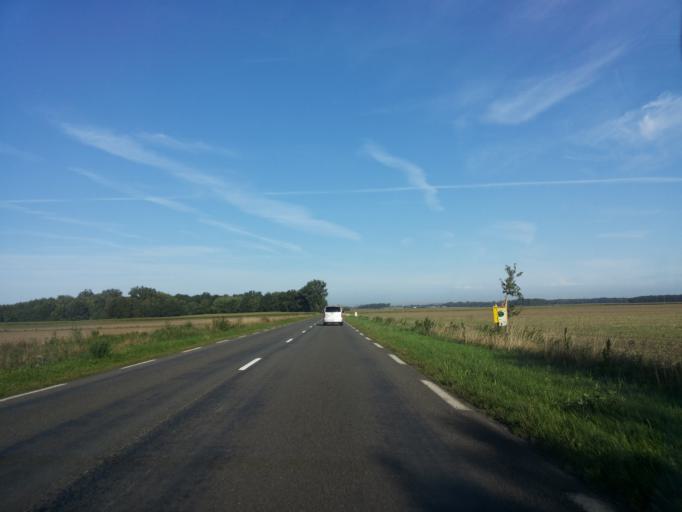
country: FR
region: Picardie
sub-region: Departement de l'Aisne
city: Athies-sous-Laon
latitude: 49.5446
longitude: 3.7321
